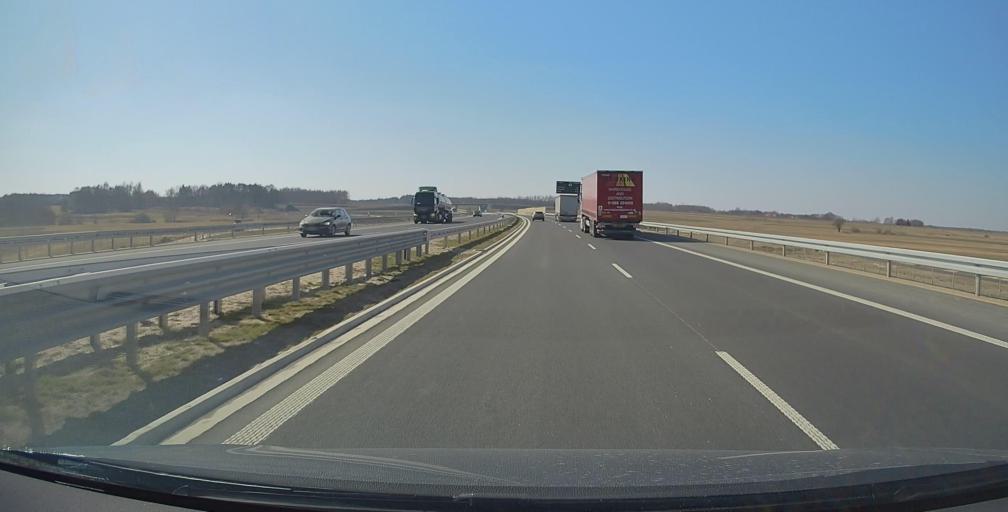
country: PL
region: Subcarpathian Voivodeship
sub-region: Powiat rzeszowski
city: Gorno
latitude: 50.2972
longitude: 22.1198
